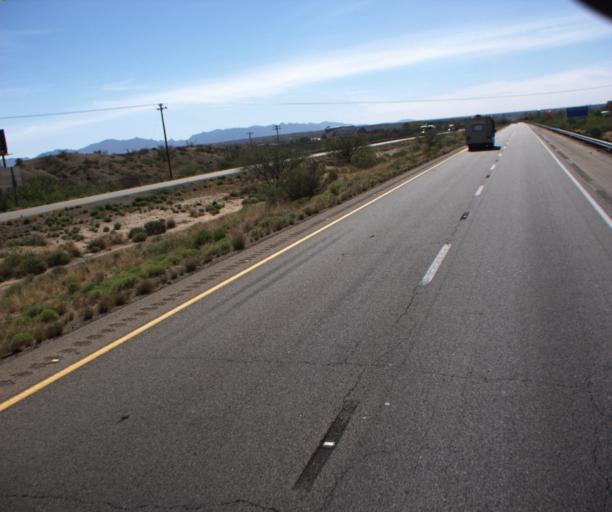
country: US
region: Arizona
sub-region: Cochise County
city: Benson
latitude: 31.9748
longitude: -110.2884
